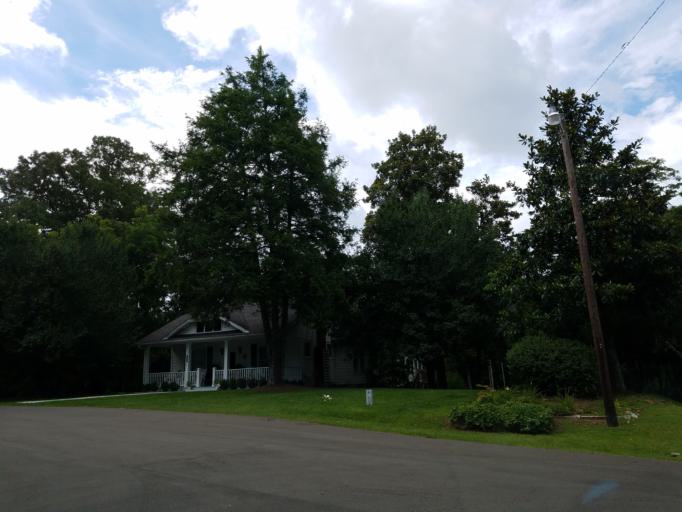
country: US
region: Georgia
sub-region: Pickens County
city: Nelson
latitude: 34.4225
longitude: -84.3913
